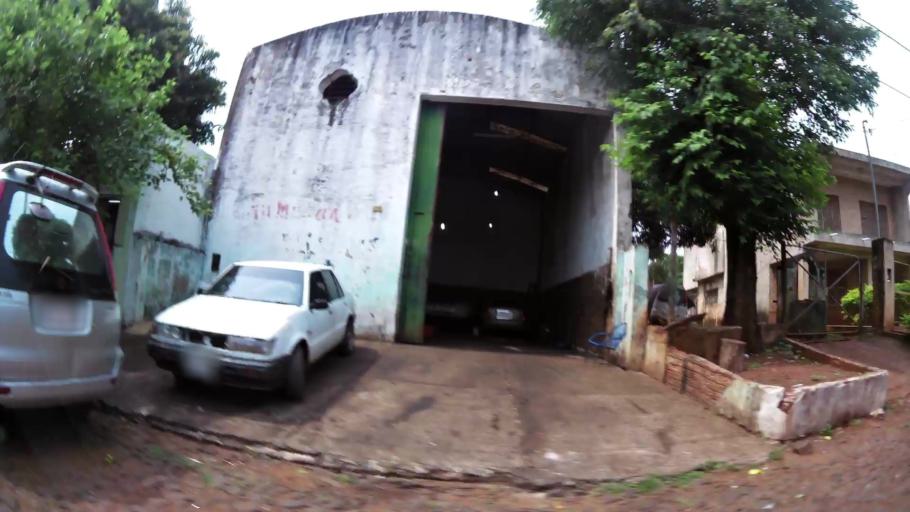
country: BR
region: Parana
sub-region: Foz Do Iguacu
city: Foz do Iguacu
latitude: -25.5551
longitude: -54.6037
